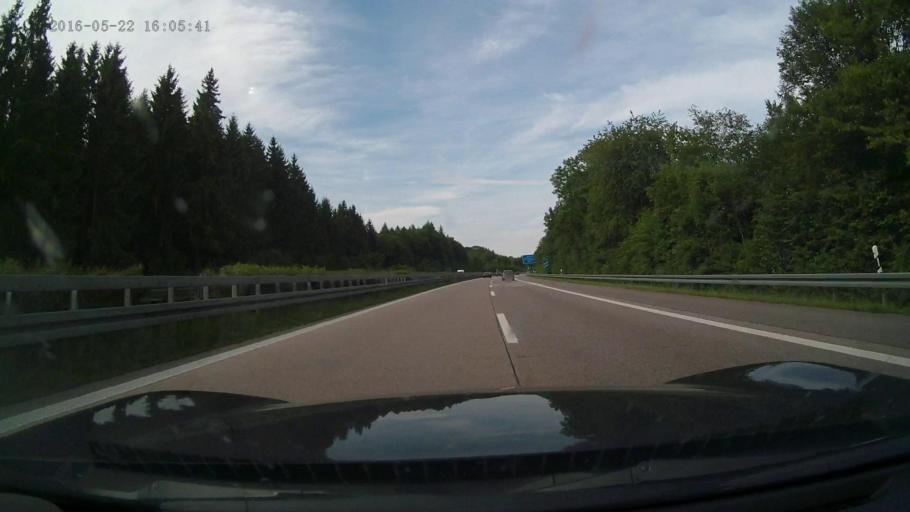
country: DE
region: Baden-Wuerttemberg
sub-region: Regierungsbezirk Stuttgart
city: Neuenstadt am Kocher
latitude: 49.2760
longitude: 9.3527
